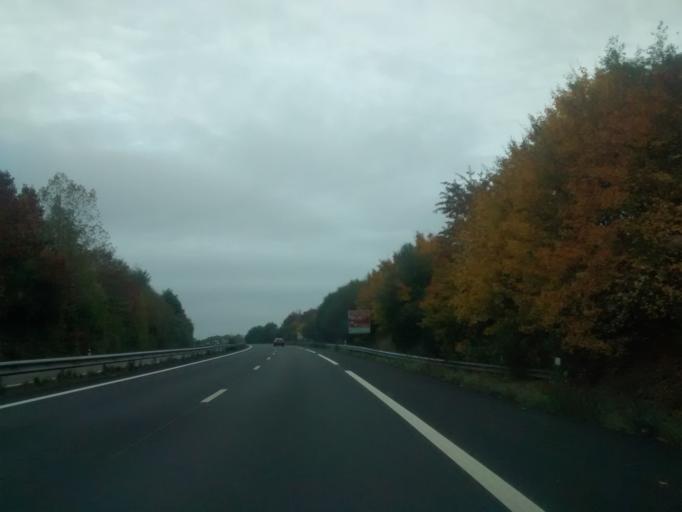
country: FR
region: Brittany
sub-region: Departement d'Ille-et-Vilaine
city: Hede-Bazouges
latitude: 48.2877
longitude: -1.8028
